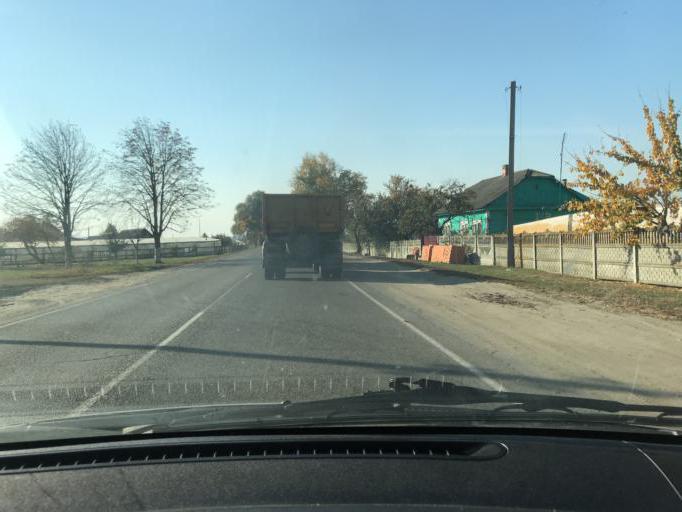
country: BY
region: Brest
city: Davyd-Haradok
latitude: 52.0599
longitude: 27.2801
